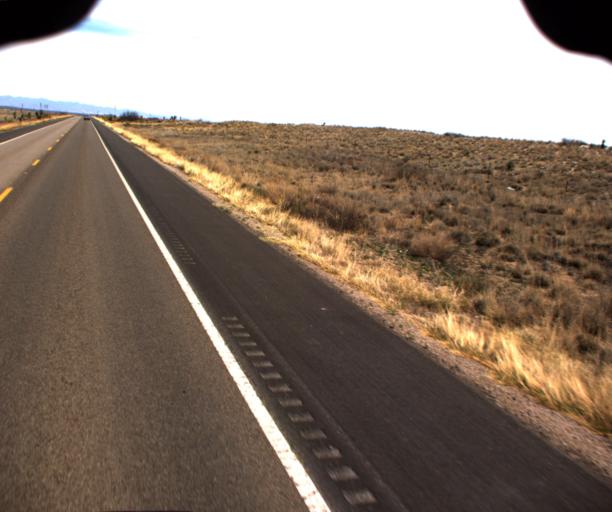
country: US
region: Arizona
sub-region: Cochise County
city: Willcox
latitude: 32.2217
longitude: -109.7910
